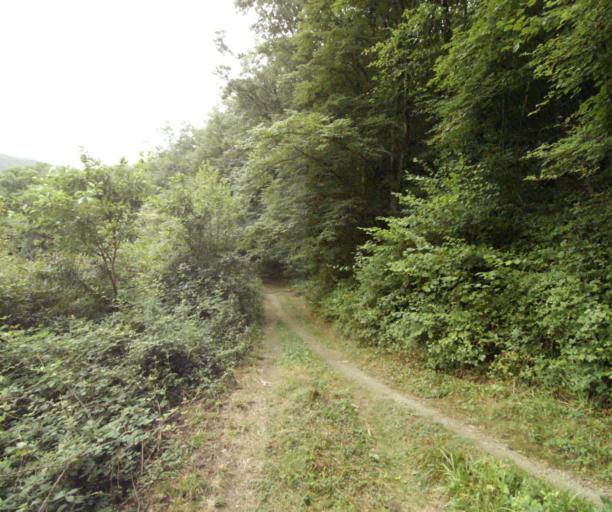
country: FR
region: Midi-Pyrenees
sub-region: Departement du Tarn
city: Soreze
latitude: 43.4399
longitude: 2.0596
